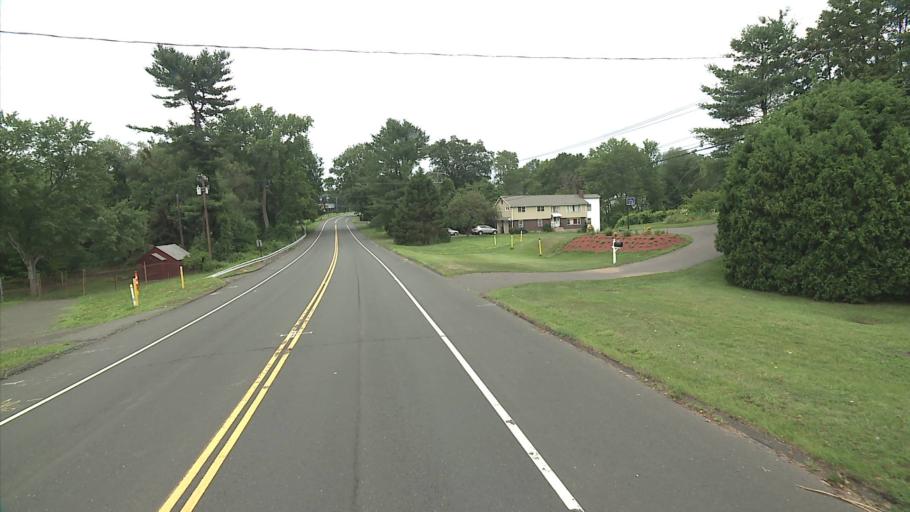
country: US
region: Connecticut
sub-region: Middlesex County
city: Cromwell
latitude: 41.6350
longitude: -72.6488
